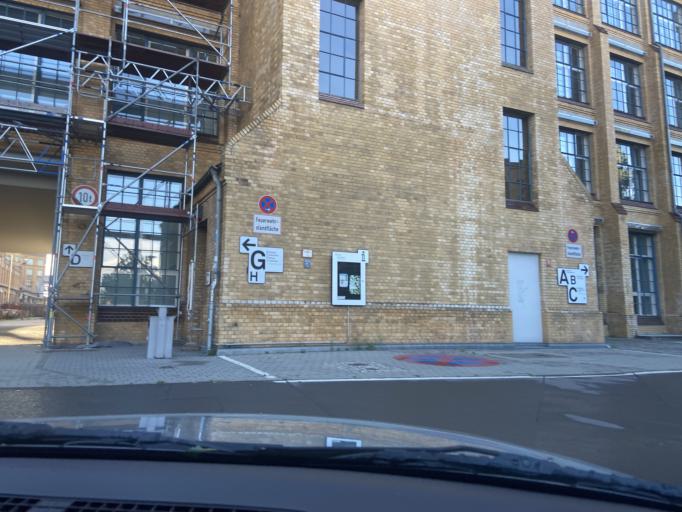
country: DE
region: Berlin
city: Oberschoneweide
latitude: 52.4561
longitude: 13.5262
